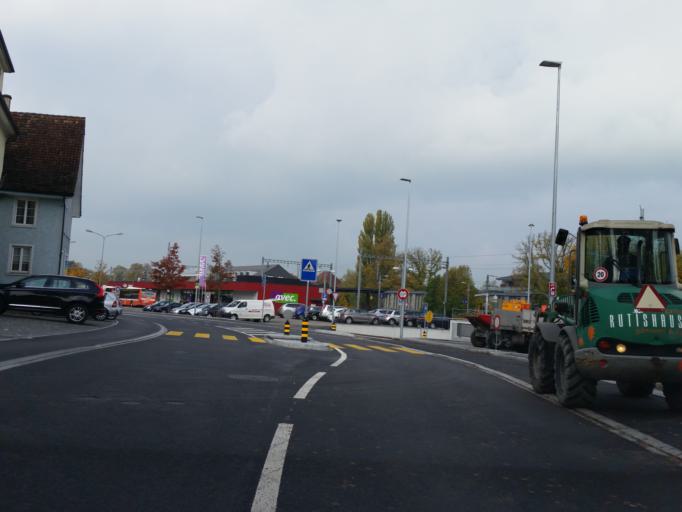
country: CH
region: Thurgau
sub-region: Arbon District
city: Amriswil
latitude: 47.5499
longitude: 9.3037
